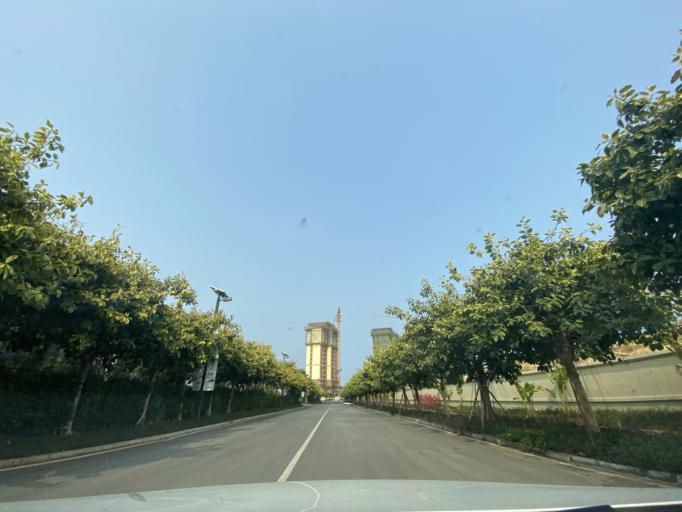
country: CN
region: Hainan
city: Yingzhou
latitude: 18.3932
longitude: 109.8520
